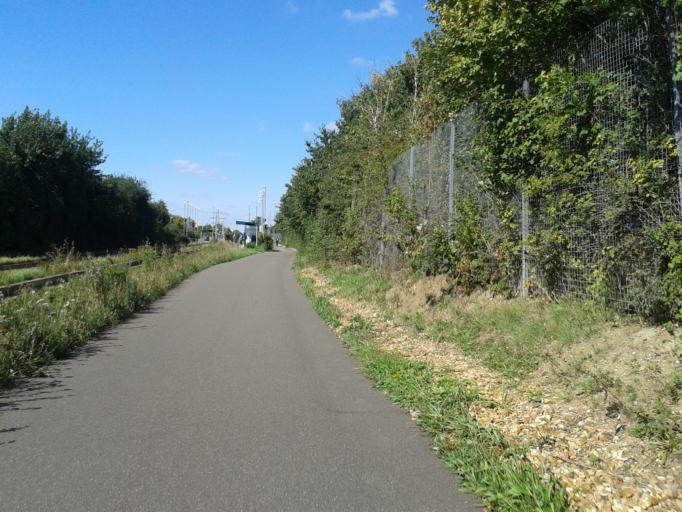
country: GB
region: England
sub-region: Cambridgeshire
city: Histon
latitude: 52.2332
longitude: 0.1380
